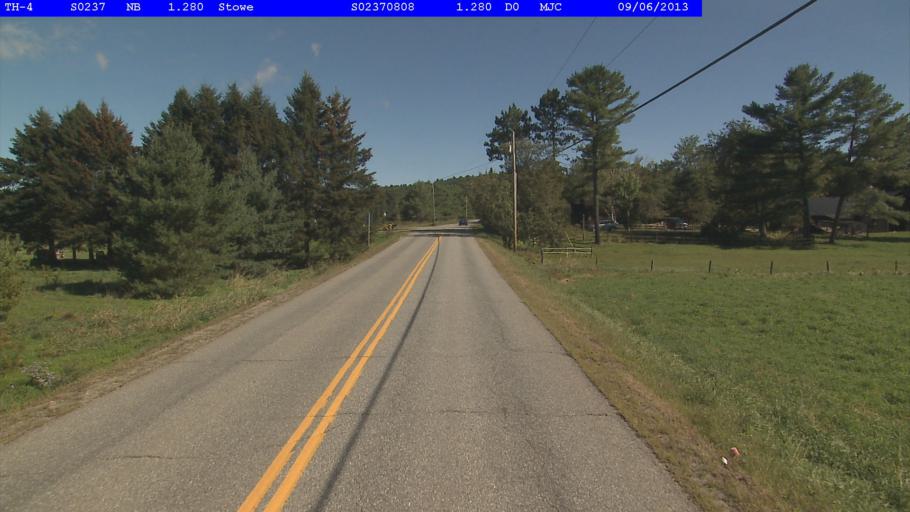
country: US
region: Vermont
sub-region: Lamoille County
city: Morristown
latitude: 44.4989
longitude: -72.6569
